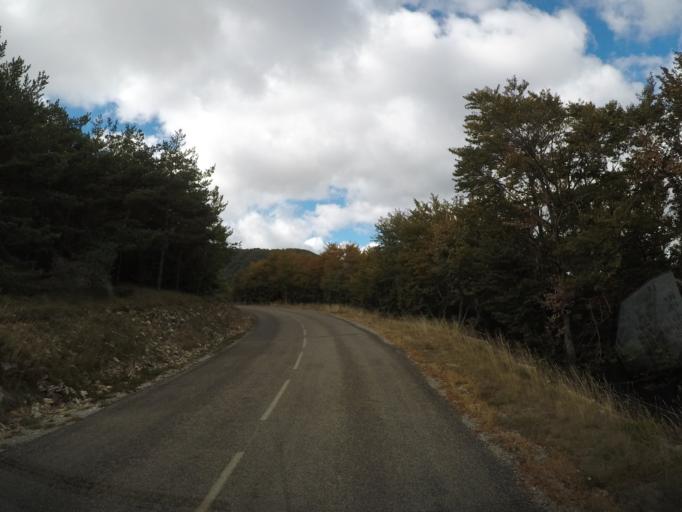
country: FR
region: Provence-Alpes-Cote d'Azur
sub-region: Departement du Vaucluse
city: Sault
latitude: 44.1728
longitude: 5.5003
